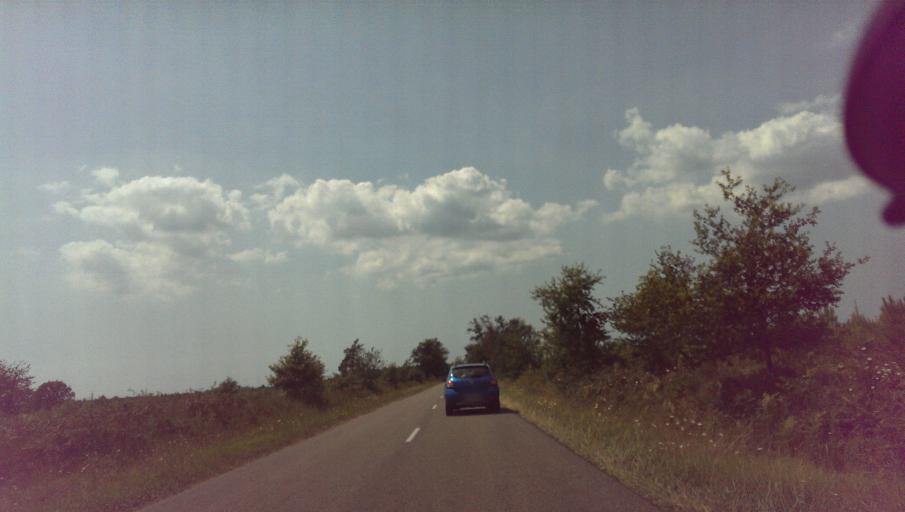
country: FR
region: Aquitaine
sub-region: Departement des Landes
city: Sabres
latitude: 44.1165
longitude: -0.6261
